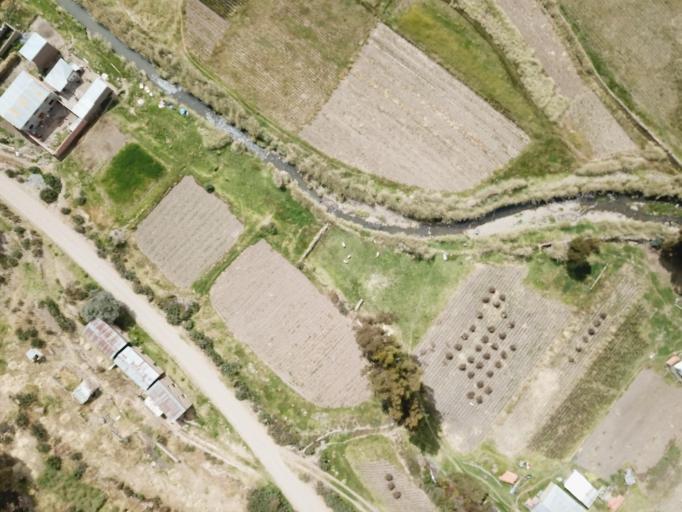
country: BO
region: La Paz
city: Achacachi
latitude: -16.0580
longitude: -68.8116
